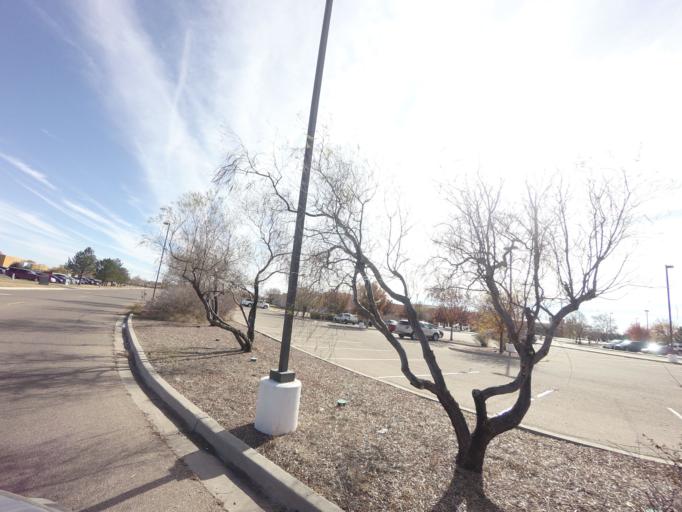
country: US
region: New Mexico
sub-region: Curry County
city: Clovis
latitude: 34.4218
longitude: -103.2352
